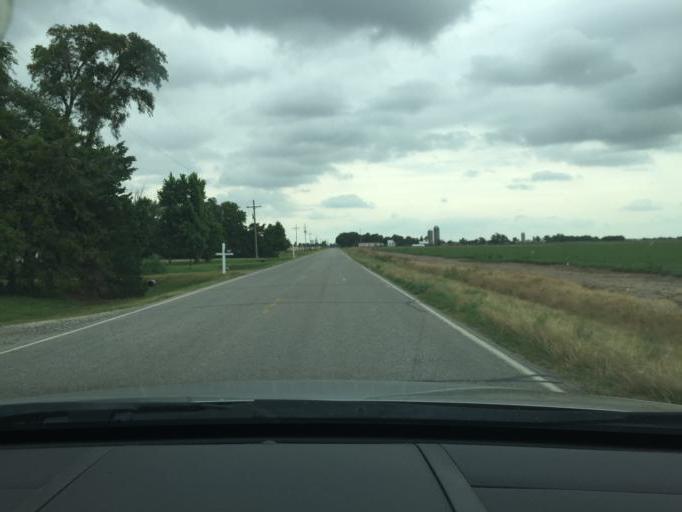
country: US
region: Kansas
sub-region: Reno County
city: South Hutchinson
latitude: 37.9749
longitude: -98.0138
